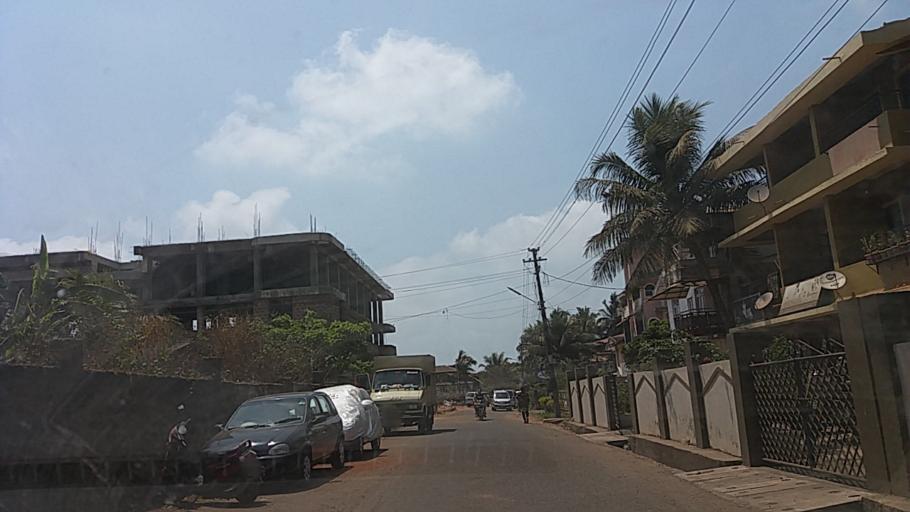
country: IN
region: Goa
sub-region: North Goa
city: Panaji
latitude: 15.5187
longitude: 73.8327
